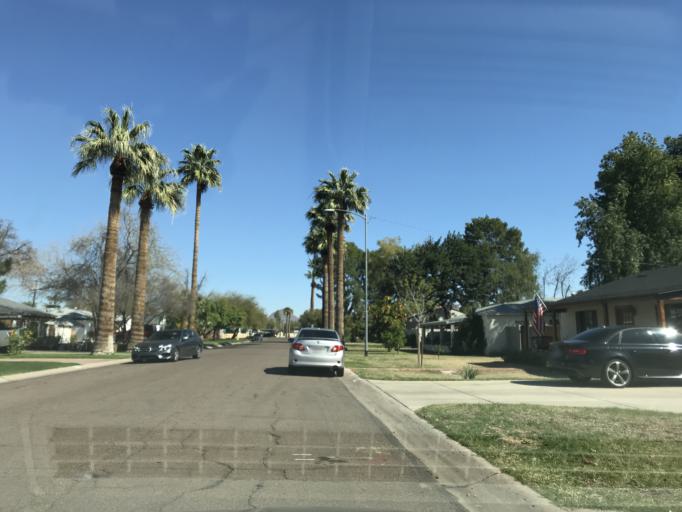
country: US
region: Arizona
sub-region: Maricopa County
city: Phoenix
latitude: 33.5137
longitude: -112.0671
